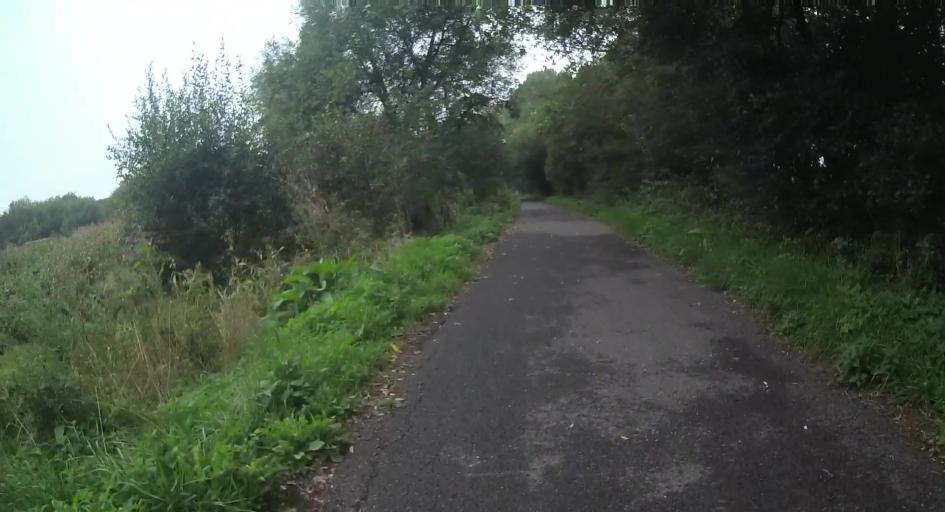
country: GB
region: England
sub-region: Isle of Wight
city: Newchurch
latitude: 50.6703
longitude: -1.1933
